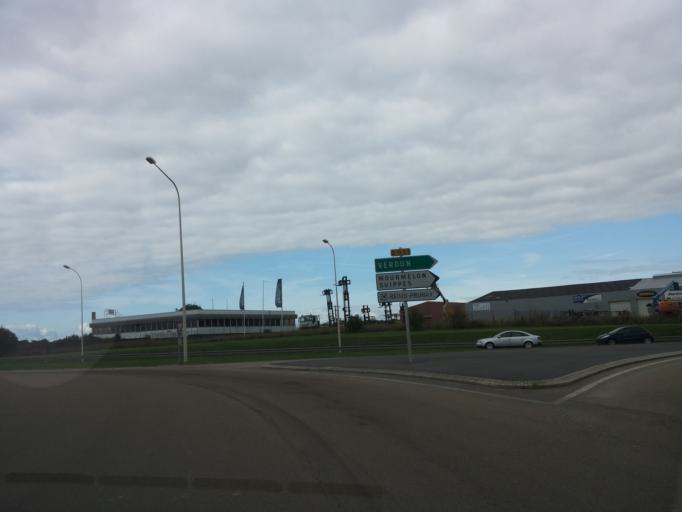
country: FR
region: Champagne-Ardenne
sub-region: Departement de la Marne
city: Sillery
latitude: 49.2091
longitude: 4.1457
